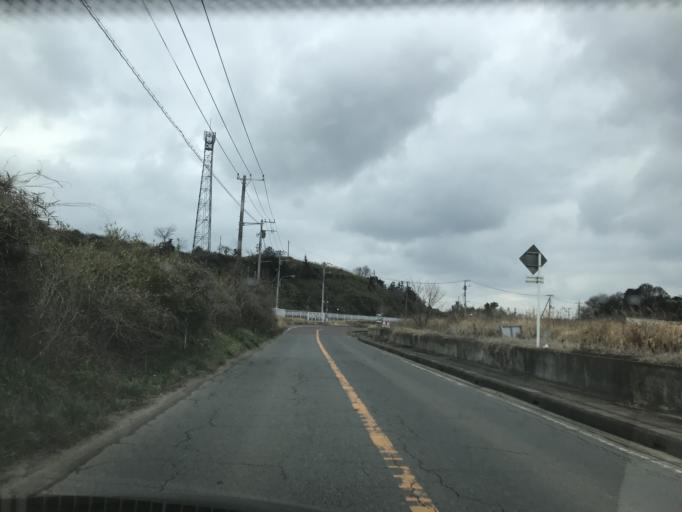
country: JP
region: Chiba
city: Sawara
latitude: 35.8345
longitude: 140.5040
